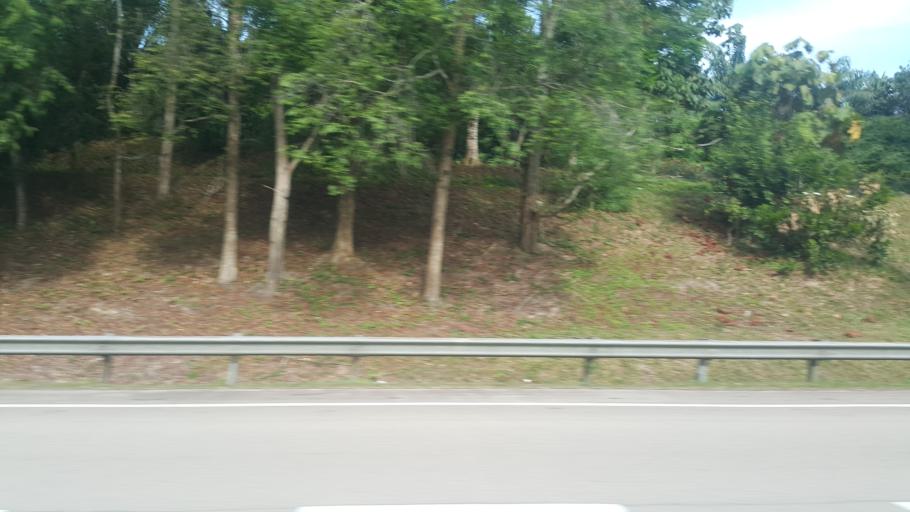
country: MY
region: Johor
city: Taman Senai
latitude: 1.5882
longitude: 103.6097
